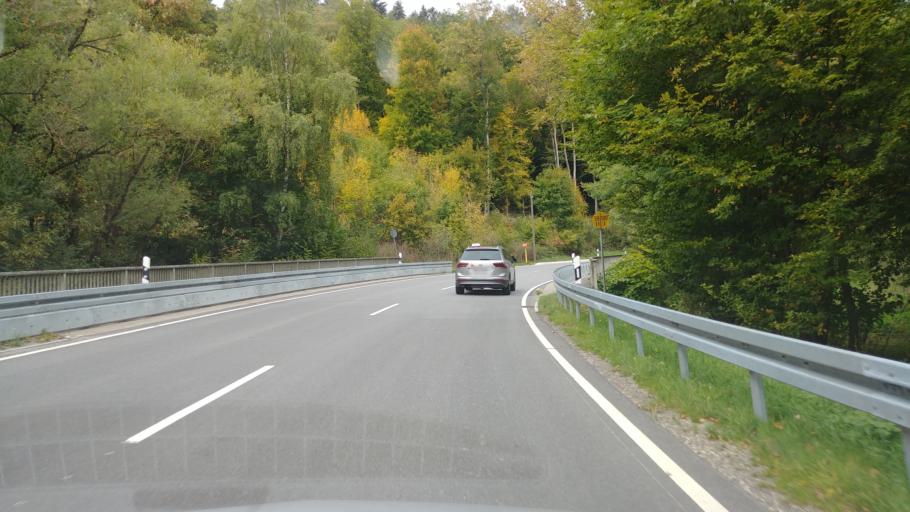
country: DE
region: Rheinland-Pfalz
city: Reckenroth
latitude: 50.2217
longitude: 8.0348
